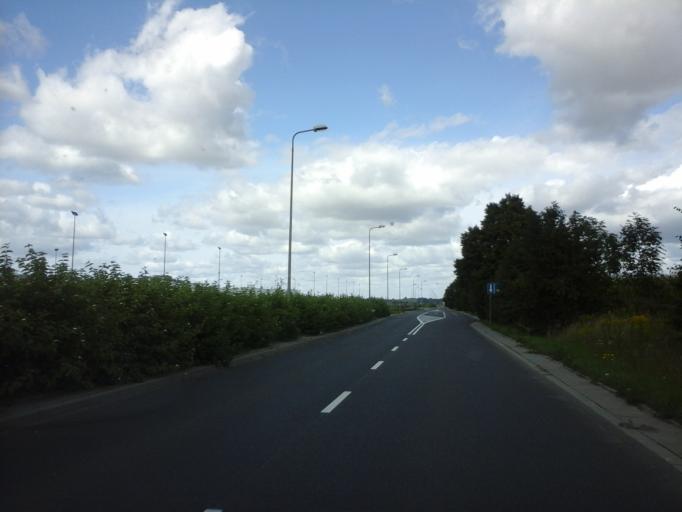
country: PL
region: West Pomeranian Voivodeship
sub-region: Powiat pyrzycki
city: Warnice
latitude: 53.3031
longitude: 14.9830
